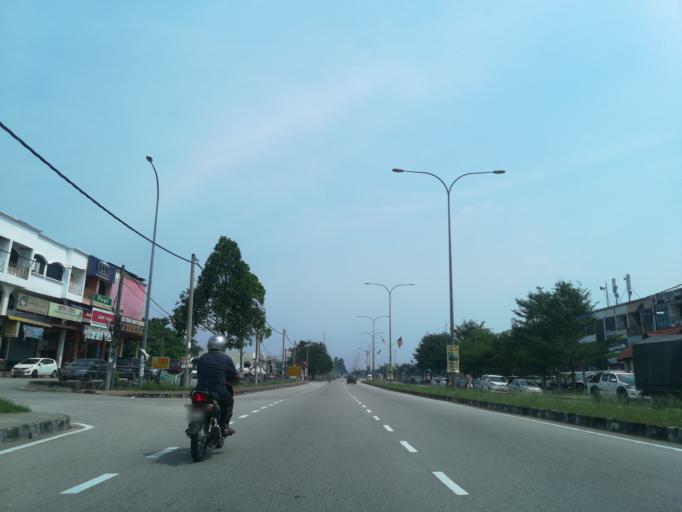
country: MY
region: Kedah
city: Kulim
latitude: 5.3963
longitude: 100.5593
